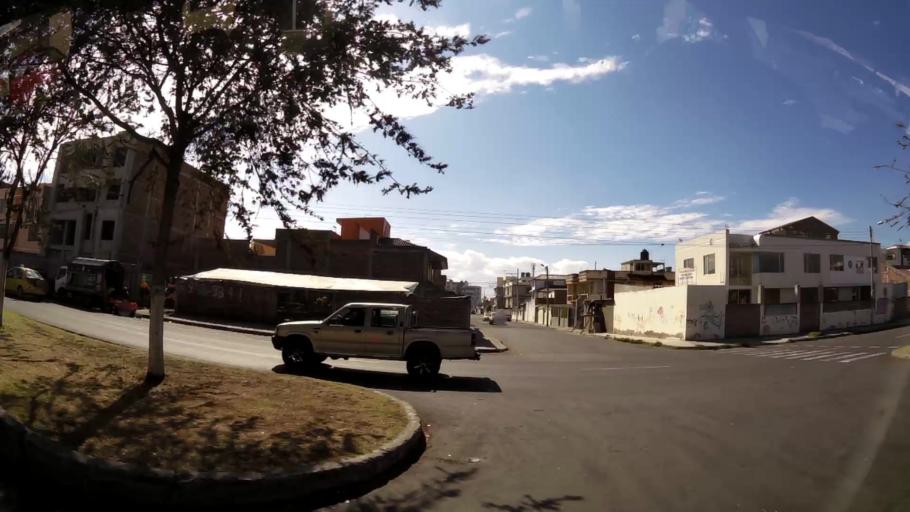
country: EC
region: Chimborazo
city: Riobamba
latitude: -1.6533
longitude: -78.6683
